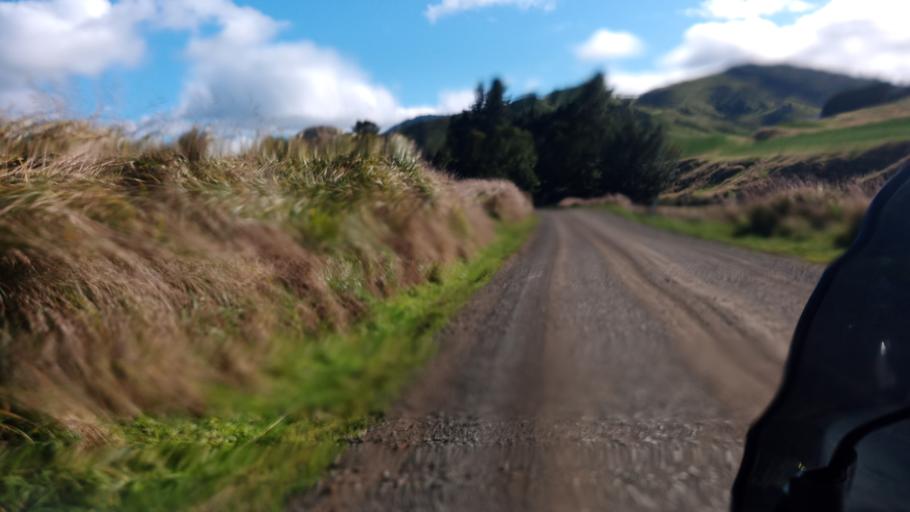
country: NZ
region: Bay of Plenty
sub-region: Opotiki District
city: Opotiki
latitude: -38.4654
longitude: 177.4270
